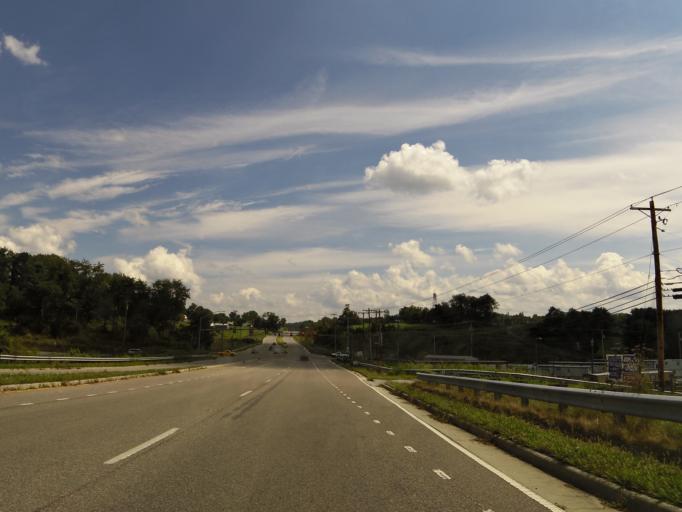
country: US
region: Virginia
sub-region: Washington County
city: Abingdon
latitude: 36.7032
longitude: -81.9154
